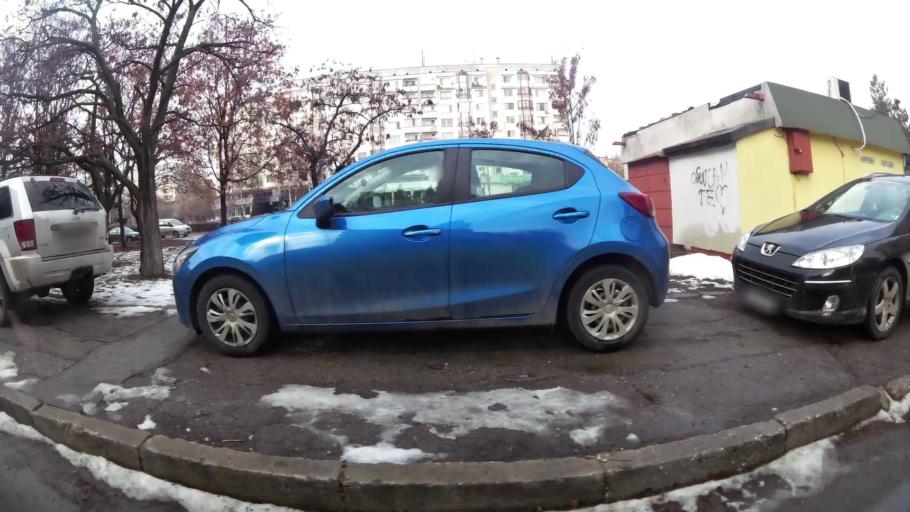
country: BG
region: Sofiya
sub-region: Obshtina Bozhurishte
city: Bozhurishte
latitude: 42.7150
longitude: 23.2507
